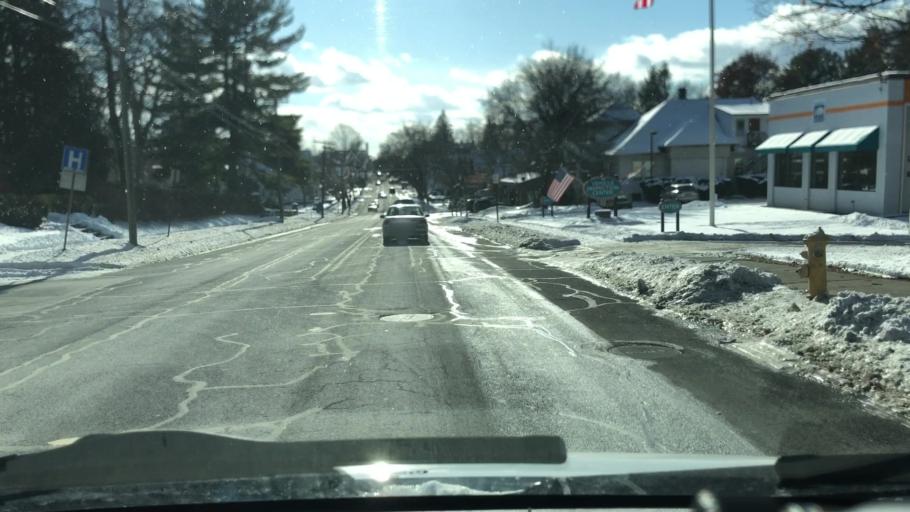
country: US
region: Massachusetts
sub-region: Franklin County
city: Greenfield
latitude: 42.5953
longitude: -72.5975
